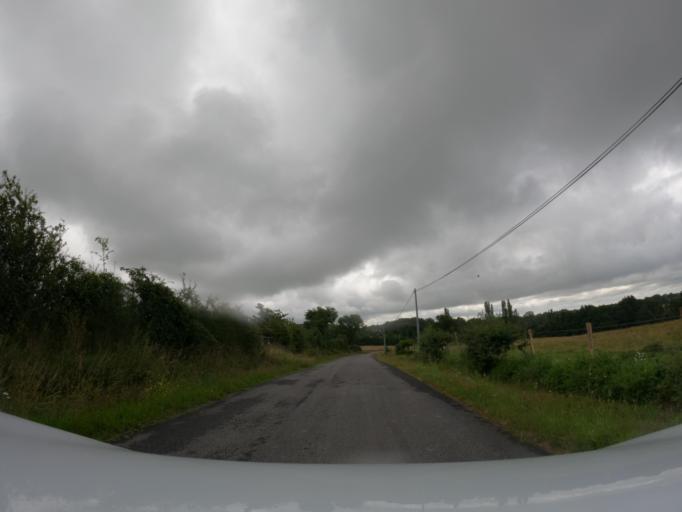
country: FR
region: Pays de la Loire
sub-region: Departement de la Loire-Atlantique
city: Saint-Mars-du-Desert
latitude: 47.3840
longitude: -1.4200
